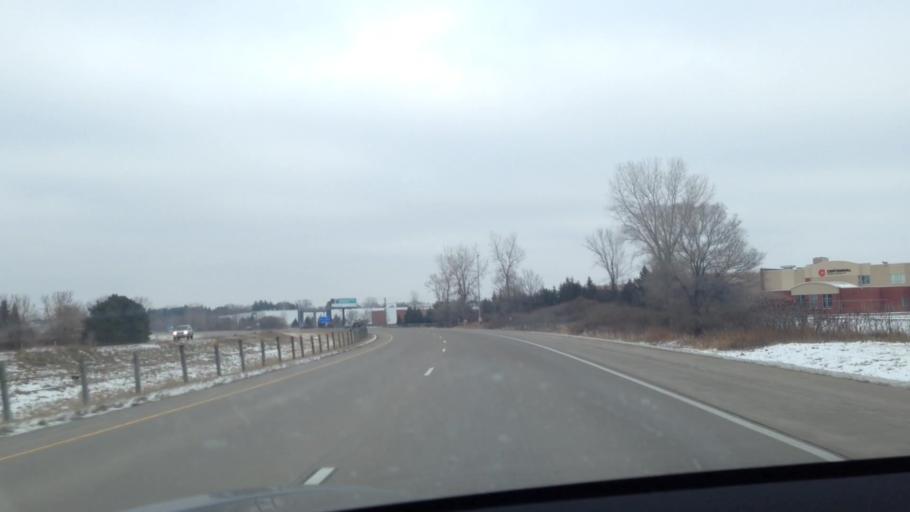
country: US
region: Minnesota
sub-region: Anoka County
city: Circle Pines
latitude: 45.1719
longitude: -93.1267
